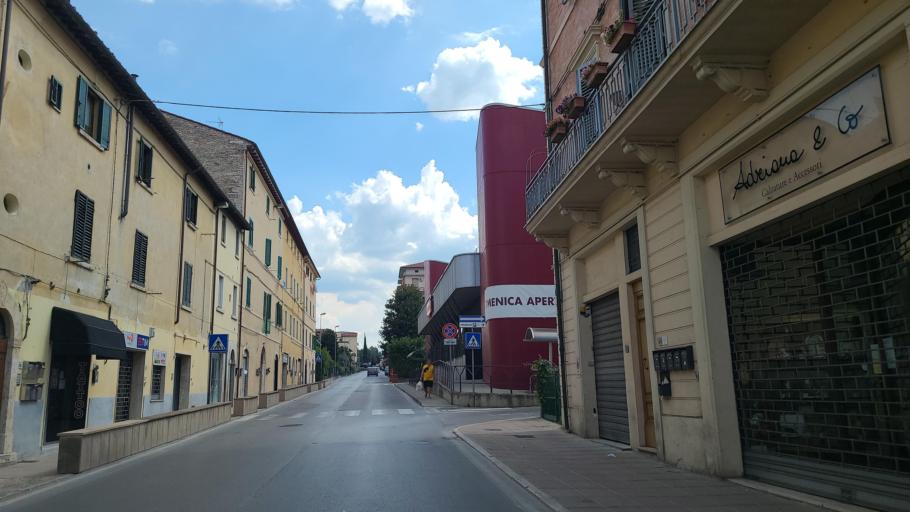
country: IT
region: Tuscany
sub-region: Provincia di Siena
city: Colle di Val d'Elsa
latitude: 43.4195
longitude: 11.1278
